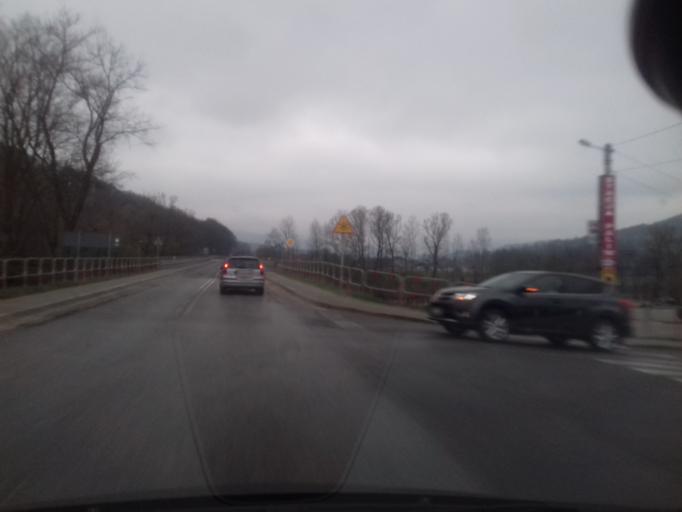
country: PL
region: Lesser Poland Voivodeship
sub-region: Powiat limanowski
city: Mszana Dolna
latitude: 49.7034
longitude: 20.0344
